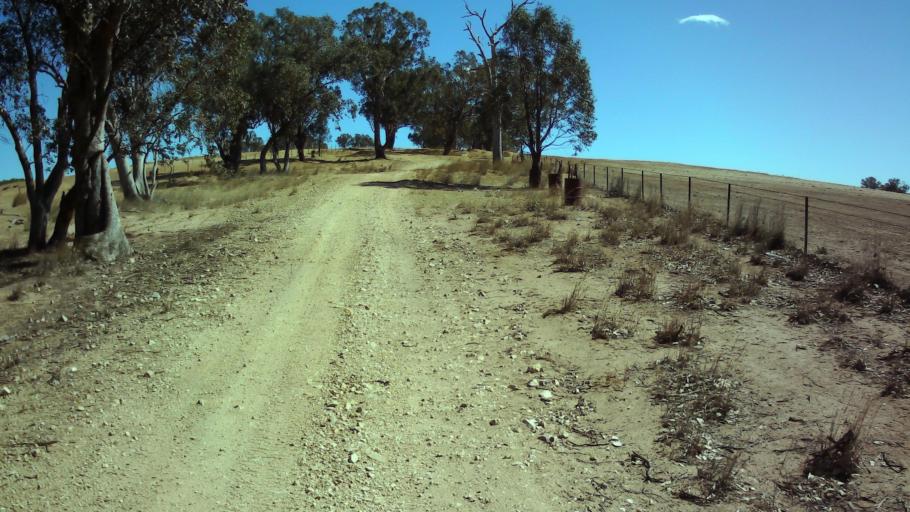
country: AU
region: New South Wales
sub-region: Weddin
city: Grenfell
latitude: -34.0000
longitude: 148.4367
